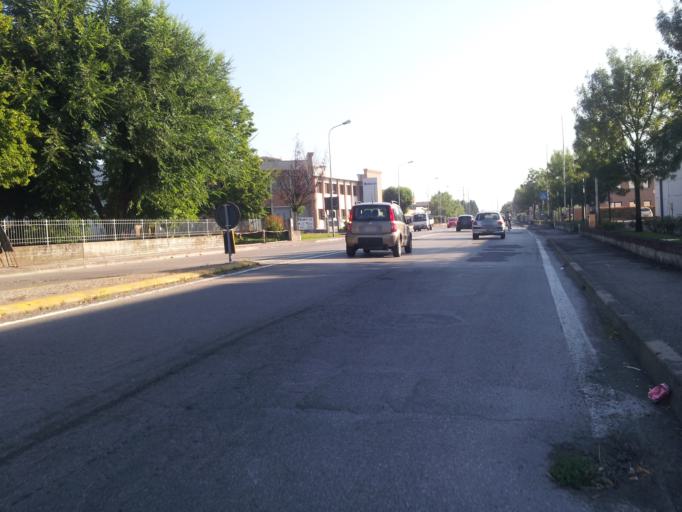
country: IT
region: Emilia-Romagna
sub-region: Provincia di Reggio Emilia
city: Reggio nell'Emilia
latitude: 44.7287
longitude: 10.6483
